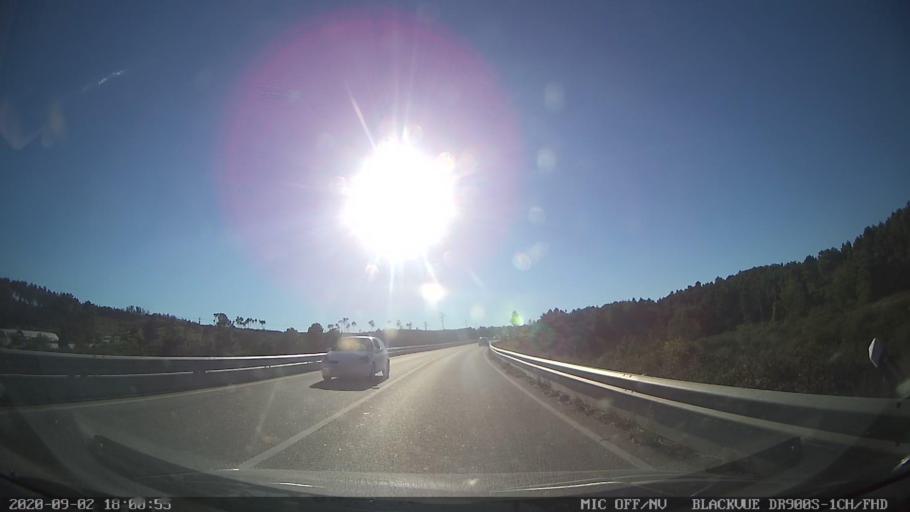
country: PT
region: Vila Real
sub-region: Sabrosa
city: Sabrosa
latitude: 41.2603
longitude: -7.6044
